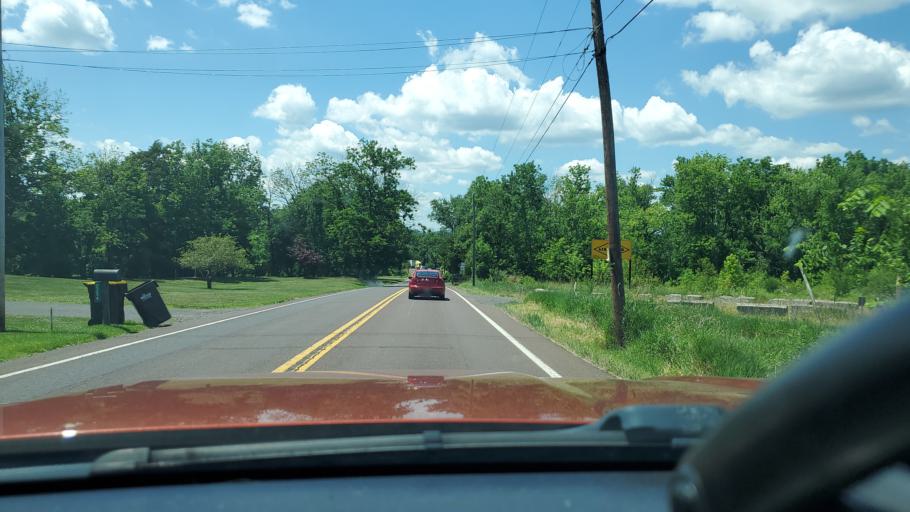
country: US
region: Pennsylvania
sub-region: Montgomery County
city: Gilbertsville
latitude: 40.3190
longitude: -75.5606
